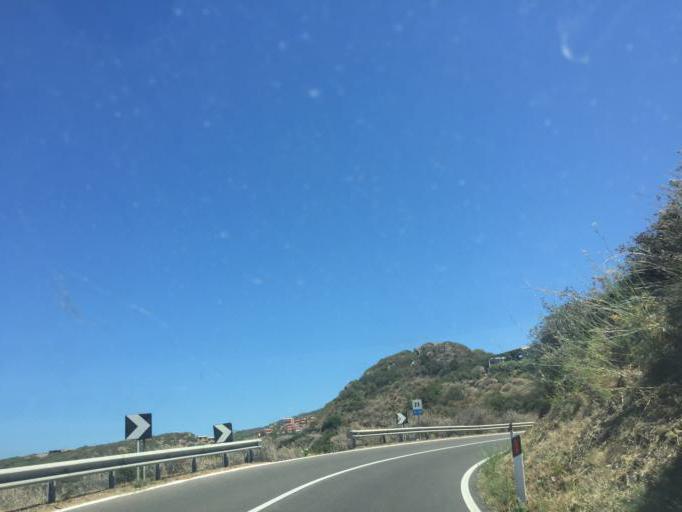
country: IT
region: Sardinia
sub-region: Provincia di Sassari
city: Castelsardo
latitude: 40.9116
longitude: 8.7258
